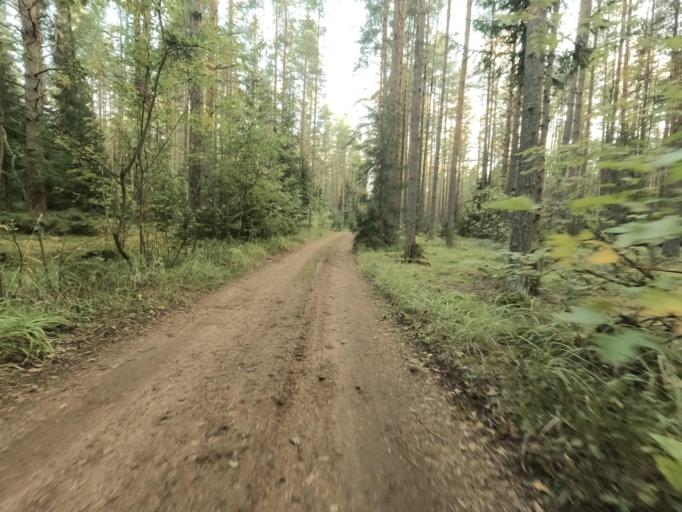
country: RU
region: Leningrad
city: Otradnoye
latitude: 59.8341
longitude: 30.7644
